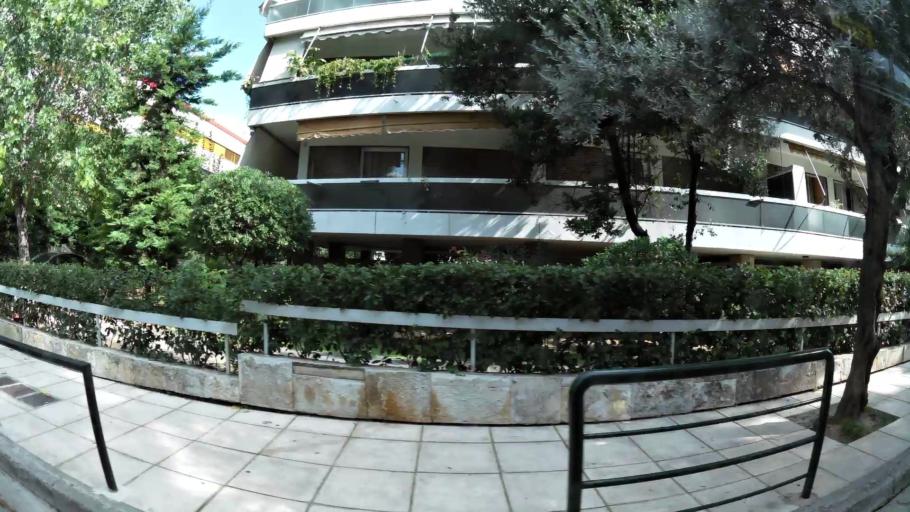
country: GR
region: Attica
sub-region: Nomarchia Athinas
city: Cholargos
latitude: 38.0052
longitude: 23.7985
